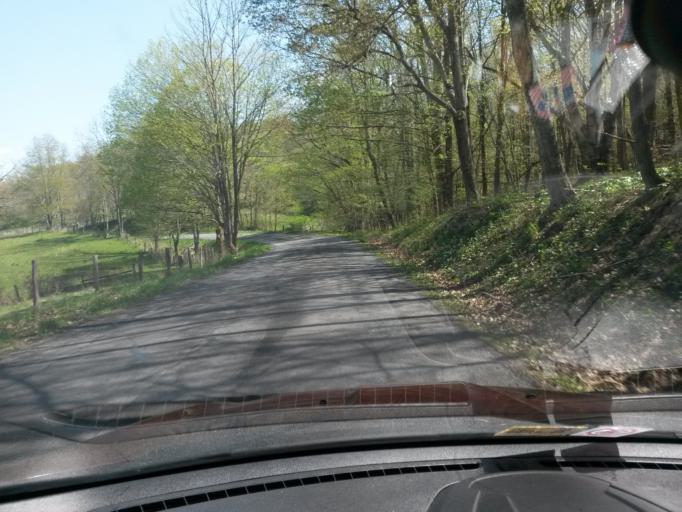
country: US
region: Virginia
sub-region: Highland County
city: Monterey
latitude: 38.2701
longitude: -79.6275
